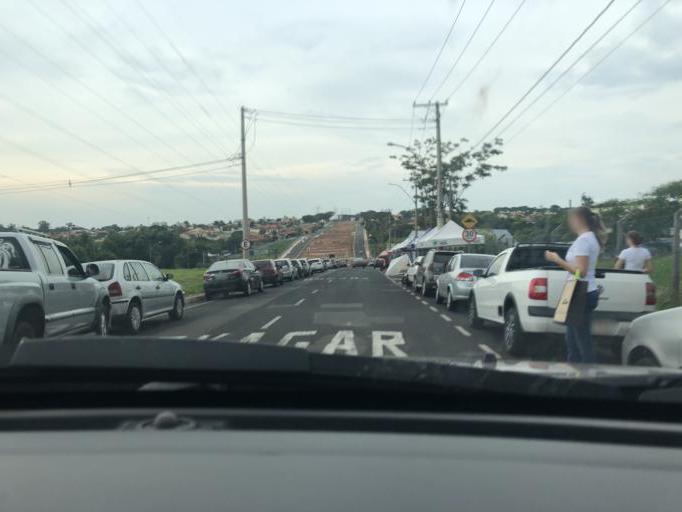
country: BR
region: Sao Paulo
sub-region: Sao Jose Do Rio Preto
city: Sao Jose do Rio Preto
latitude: -20.8423
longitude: -49.4141
